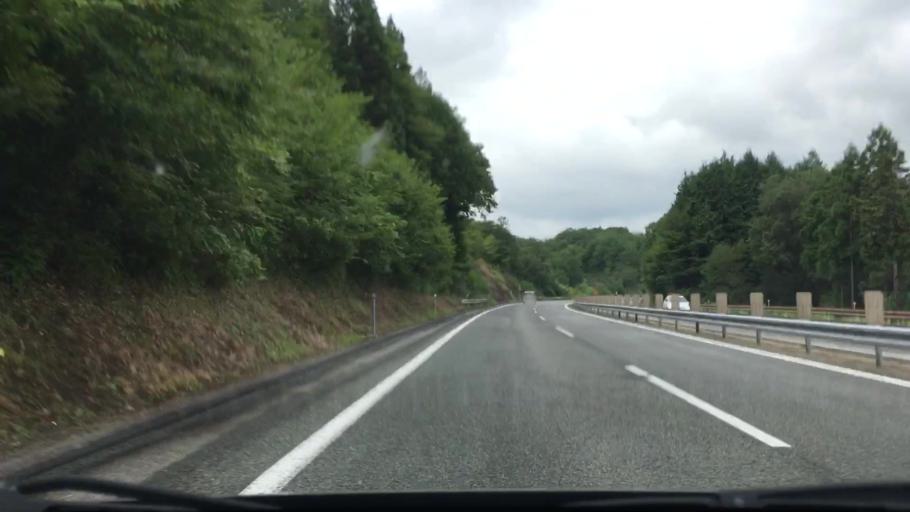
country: JP
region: Hiroshima
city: Miyoshi
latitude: 34.7548
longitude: 132.7402
